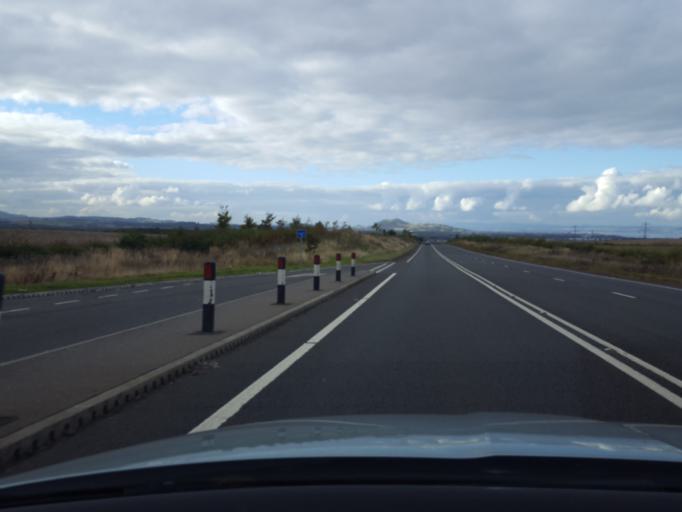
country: GB
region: Scotland
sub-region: Fife
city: Pathhead
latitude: 55.8975
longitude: -3.0133
